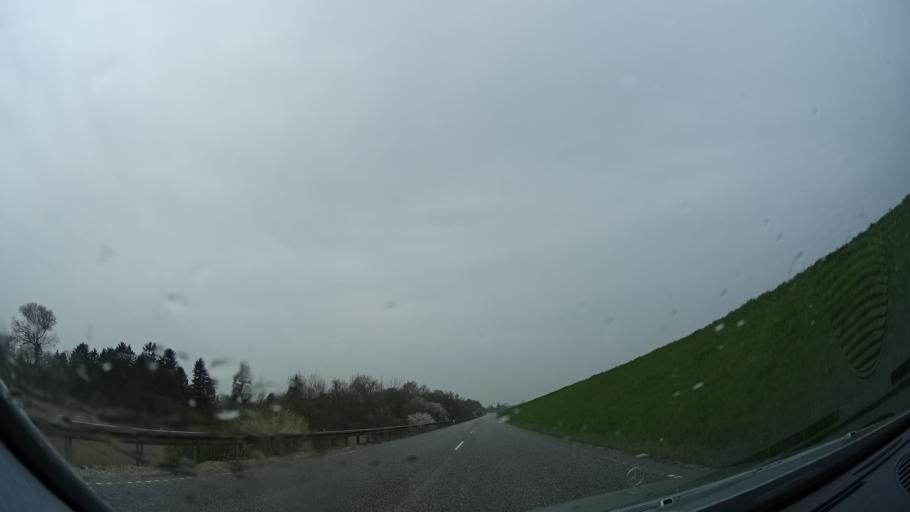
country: DK
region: Zealand
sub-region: Holbaek Kommune
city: Holbaek
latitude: 55.7762
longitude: 11.6182
